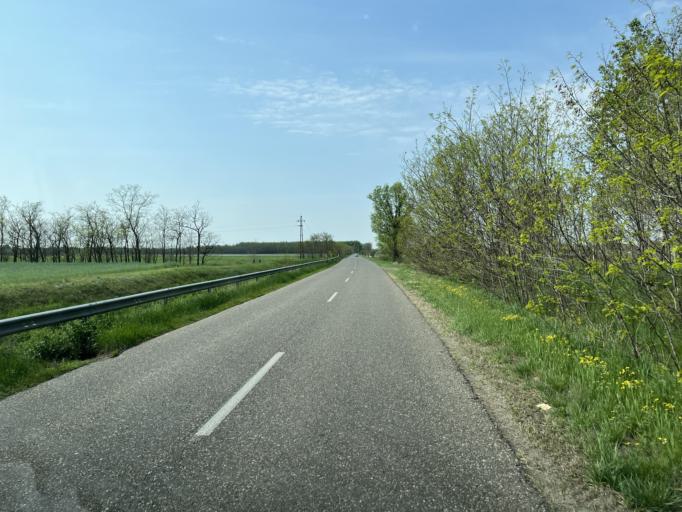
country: HU
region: Pest
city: Tortel
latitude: 47.1076
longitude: 19.9103
